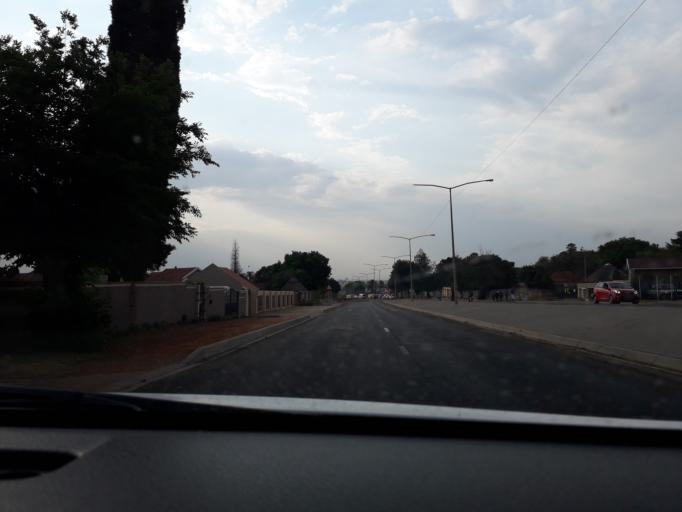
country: ZA
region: Gauteng
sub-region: City of Johannesburg Metropolitan Municipality
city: Modderfontein
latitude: -26.0606
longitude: 28.2050
